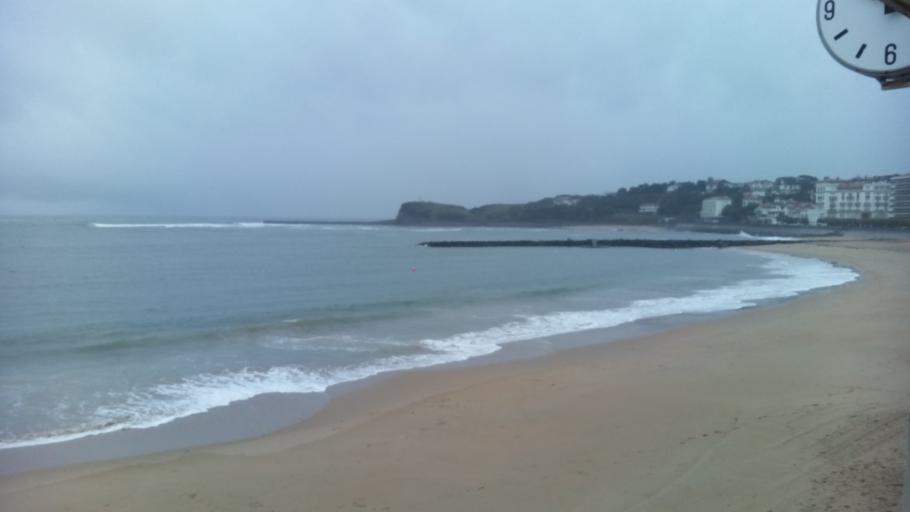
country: FR
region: Aquitaine
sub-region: Departement des Pyrenees-Atlantiques
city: Saint-Jean-de-Luz
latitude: 43.3915
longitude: -1.6614
